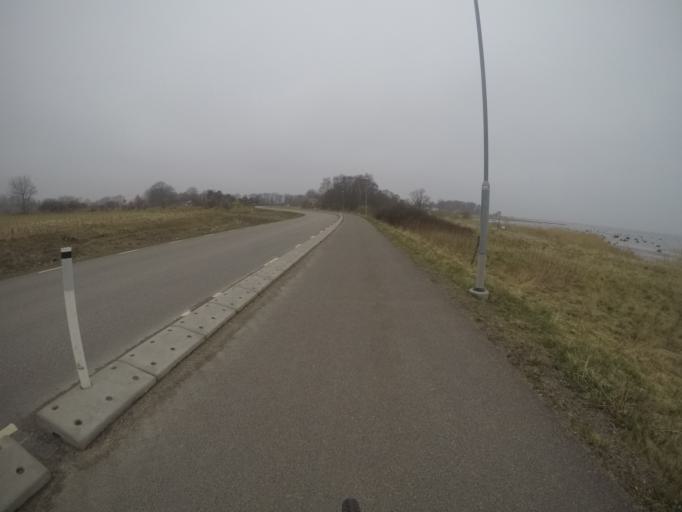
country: SE
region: Skane
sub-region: Angelholms Kommun
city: Strovelstorp
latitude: 56.2188
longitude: 12.7673
